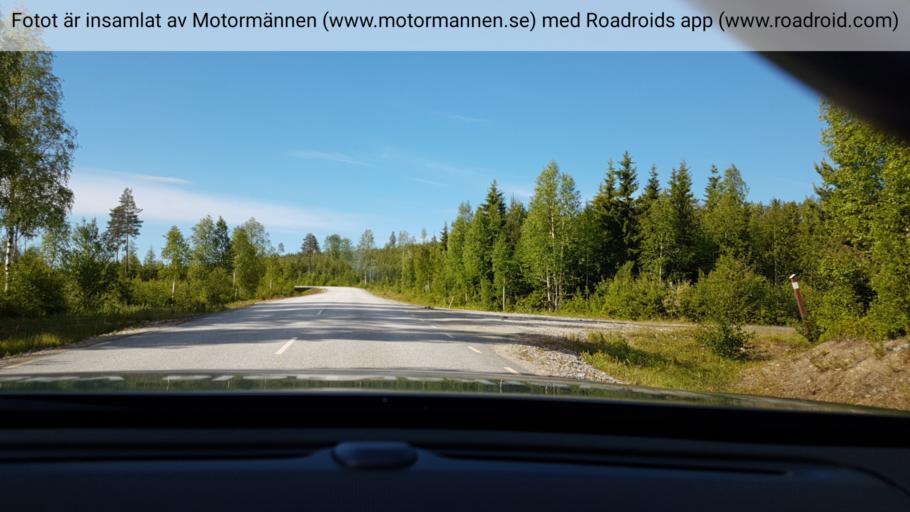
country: SE
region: Vaesterbotten
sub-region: Vindelns Kommun
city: Vindeln
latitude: 64.1874
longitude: 19.4039
